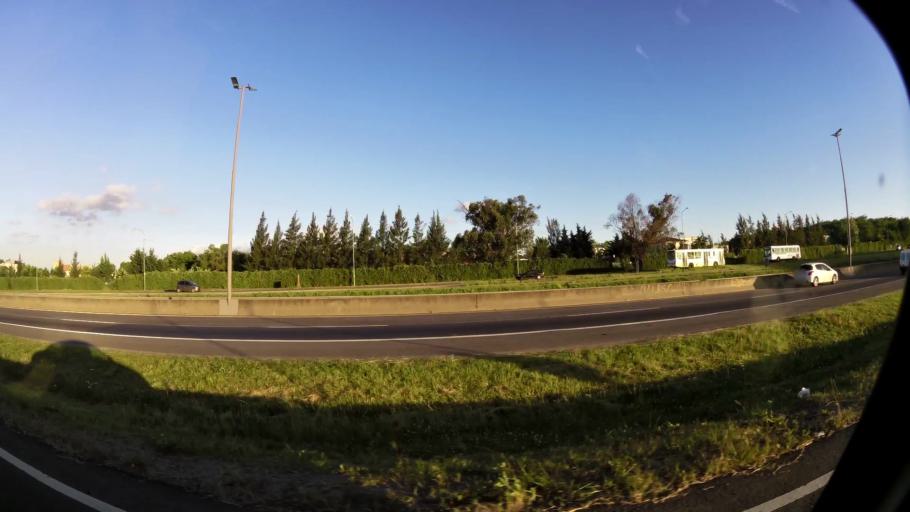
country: AR
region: Buenos Aires
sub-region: Partido de Quilmes
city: Quilmes
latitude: -34.7936
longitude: -58.1592
